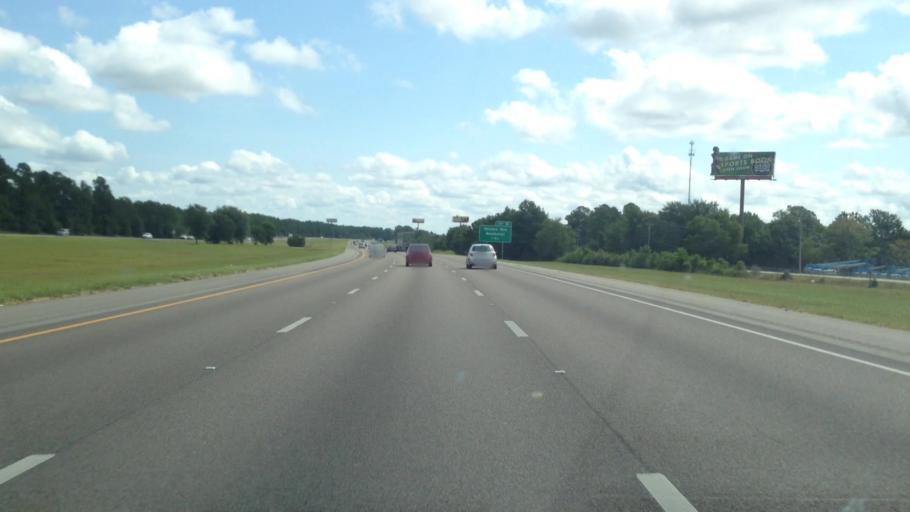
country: US
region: Mississippi
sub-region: Harrison County
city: D'Iberville
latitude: 30.4522
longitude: -88.9916
